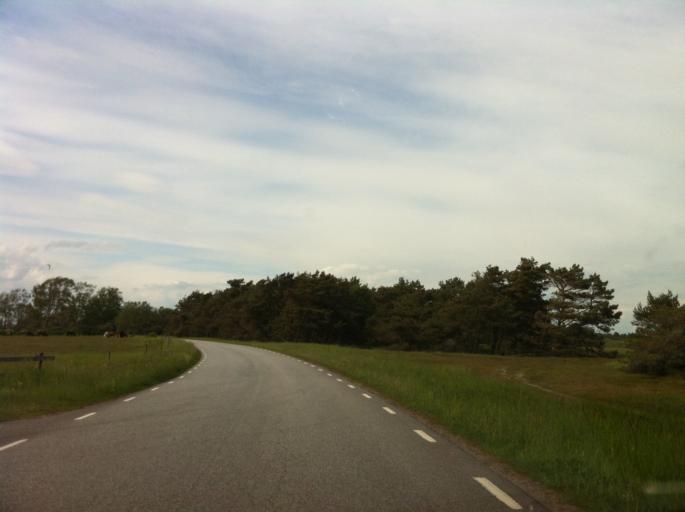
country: SE
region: Skane
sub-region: Kavlinge Kommun
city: Hofterup
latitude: 55.8125
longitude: 12.9367
